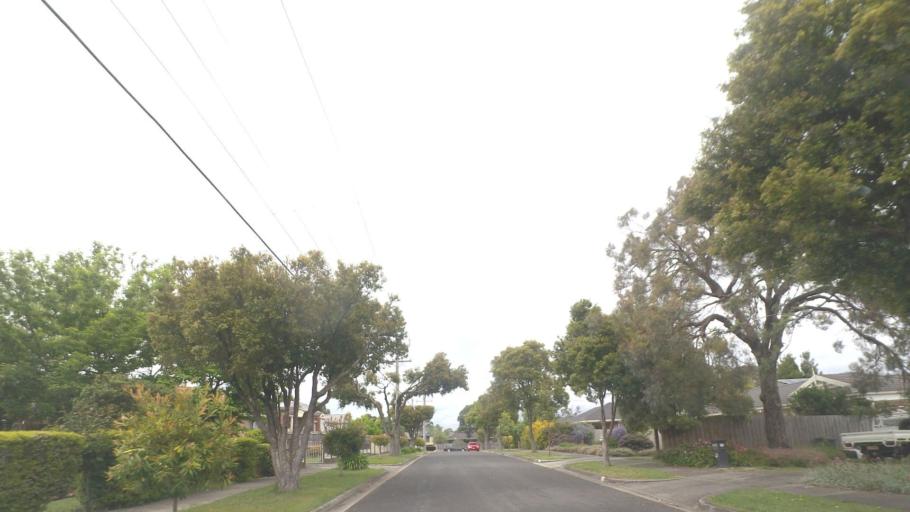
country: AU
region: Victoria
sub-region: Maroondah
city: Croydon South
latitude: -37.8129
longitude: 145.2736
